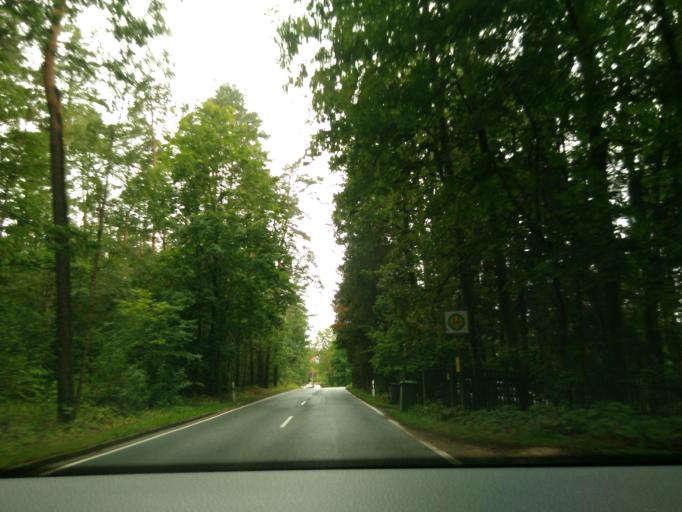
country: DE
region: Bavaria
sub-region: Regierungsbezirk Mittelfranken
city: Cadolzburg
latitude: 49.4574
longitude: 10.8715
